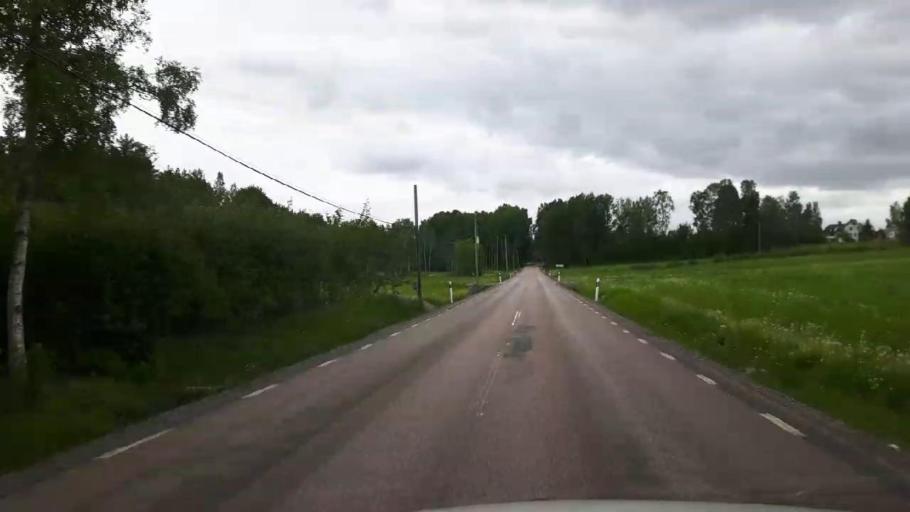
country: SE
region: Vaestmanland
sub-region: Kopings Kommun
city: Kolsva
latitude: 59.7082
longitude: 15.7970
